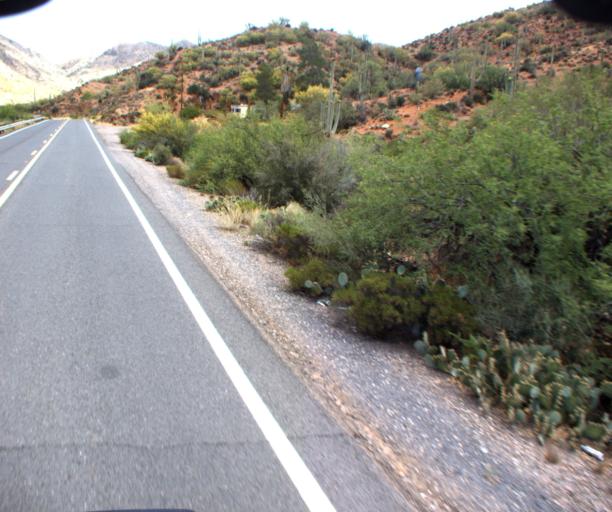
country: US
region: Arizona
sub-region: Pinal County
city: Superior
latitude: 33.1897
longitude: -111.0444
